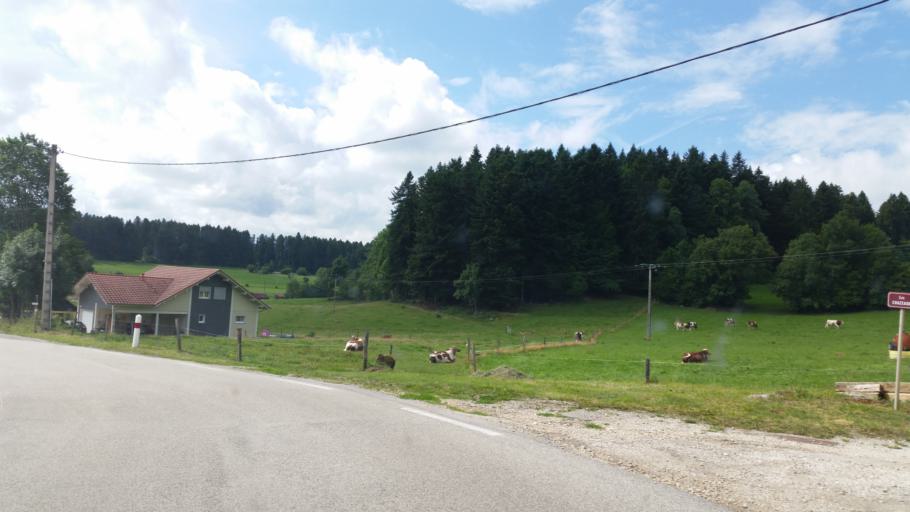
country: FR
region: Franche-Comte
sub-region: Departement du Doubs
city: Charquemont
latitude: 47.1667
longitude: 6.8275
